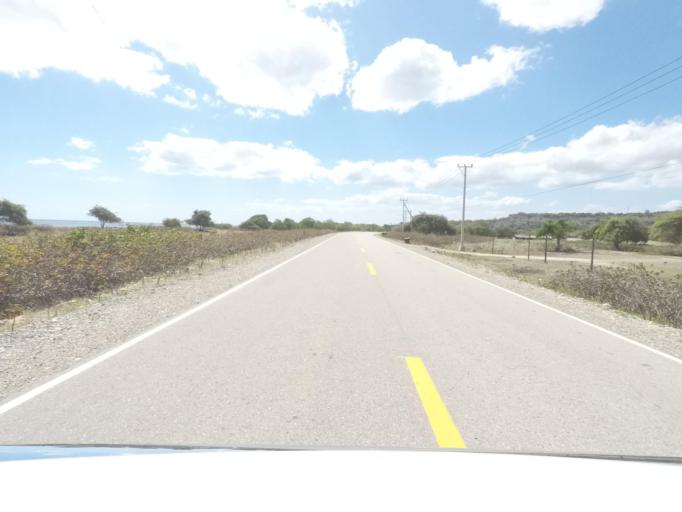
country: TL
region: Baucau
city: Baucau
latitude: -8.4428
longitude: 126.6514
